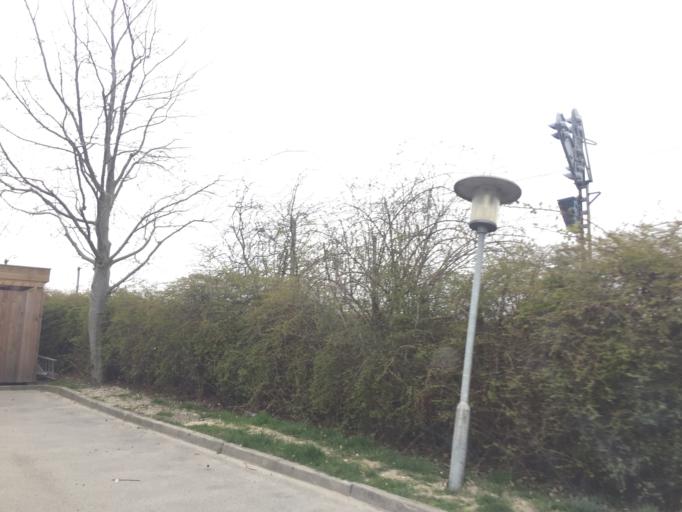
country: DK
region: Capital Region
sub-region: Kobenhavn
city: Copenhagen
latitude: 55.7167
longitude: 12.5632
